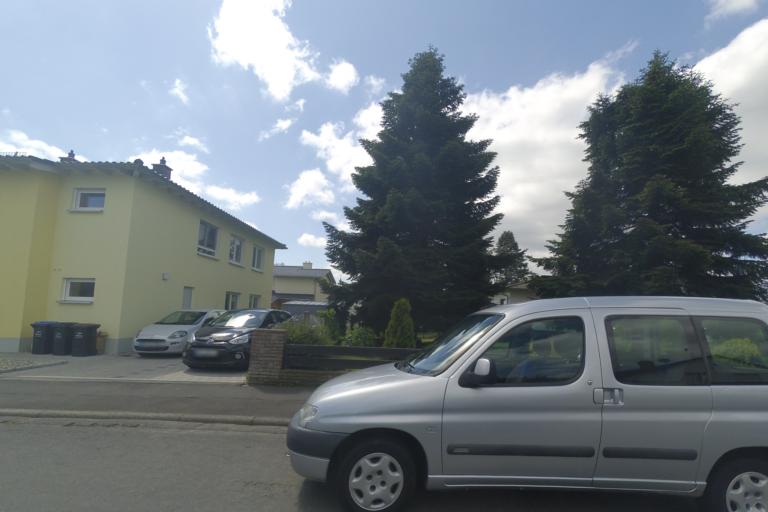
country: DE
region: Hesse
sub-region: Regierungsbezirk Darmstadt
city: Rosbach vor der Hohe
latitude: 50.2632
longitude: 8.7051
